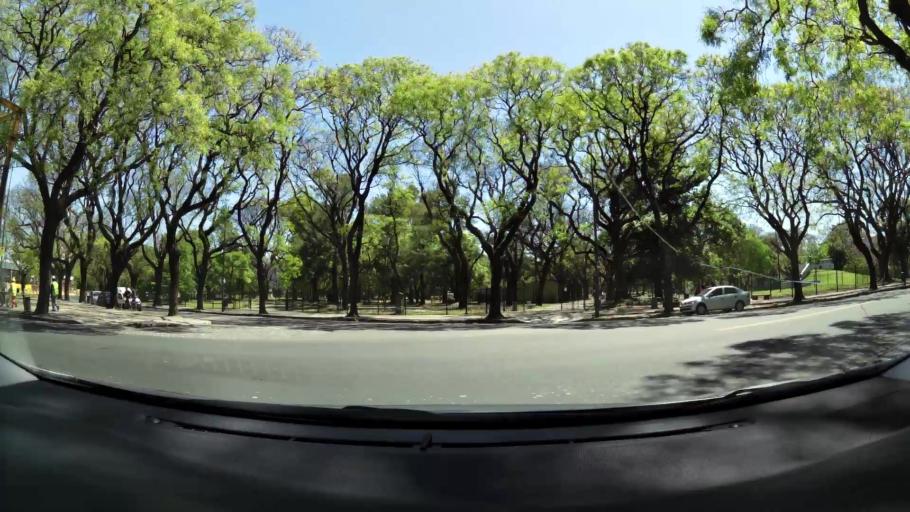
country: AR
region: Buenos Aires F.D.
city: Buenos Aires
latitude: -34.6401
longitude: -58.4078
